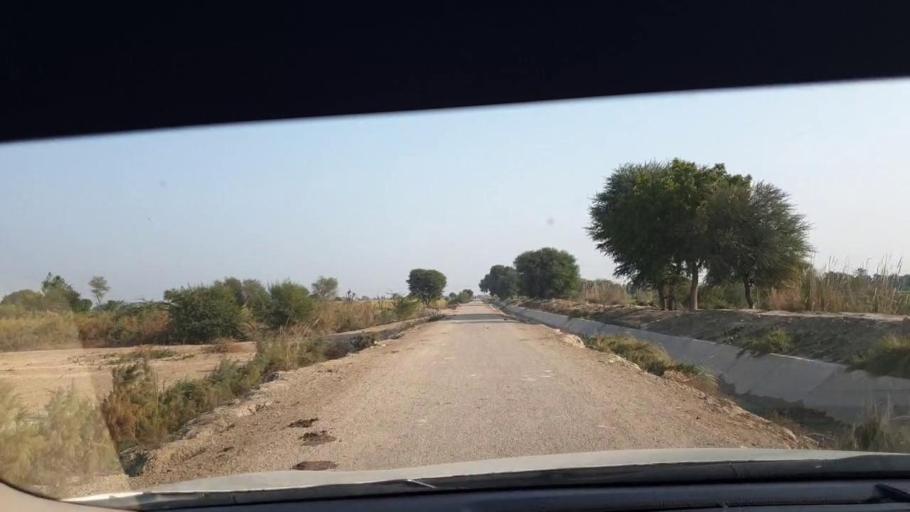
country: PK
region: Sindh
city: Berani
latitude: 25.8337
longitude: 68.7740
